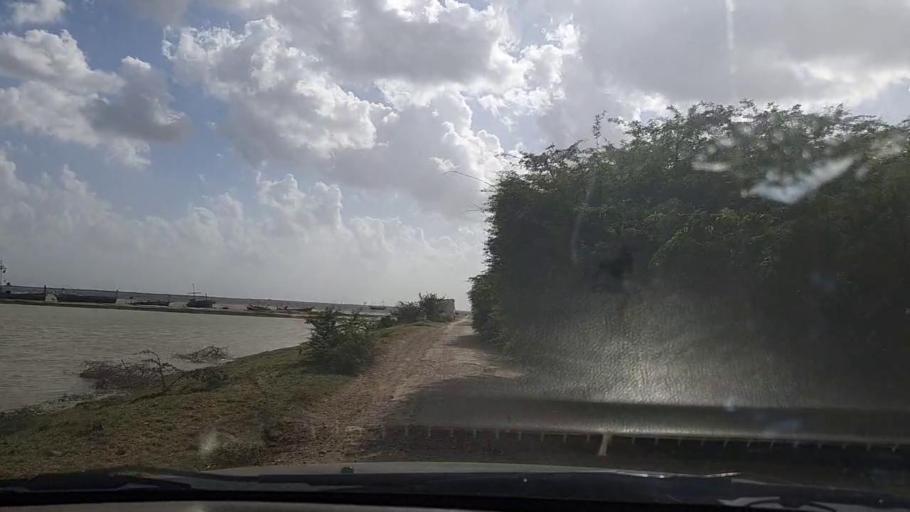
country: PK
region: Sindh
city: Keti Bandar
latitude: 24.0858
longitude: 67.6150
